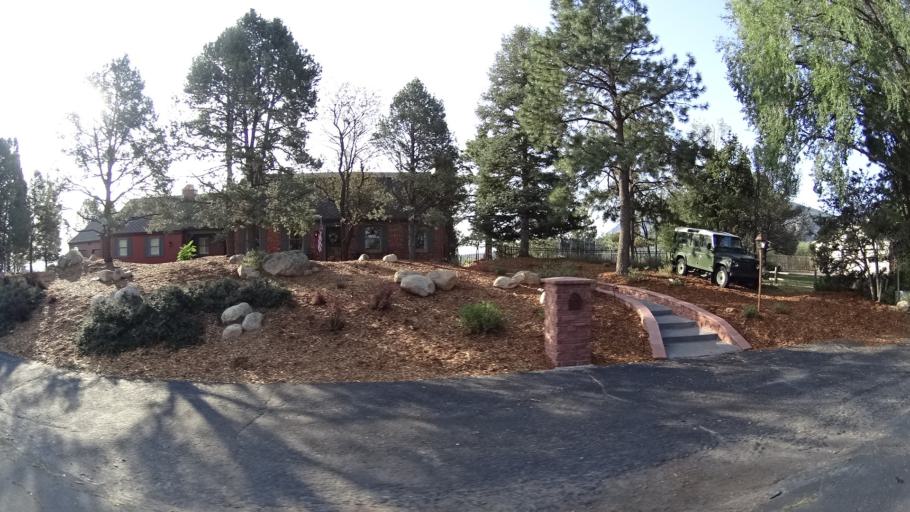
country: US
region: Colorado
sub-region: El Paso County
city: Colorado Springs
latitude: 38.8082
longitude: -104.8566
